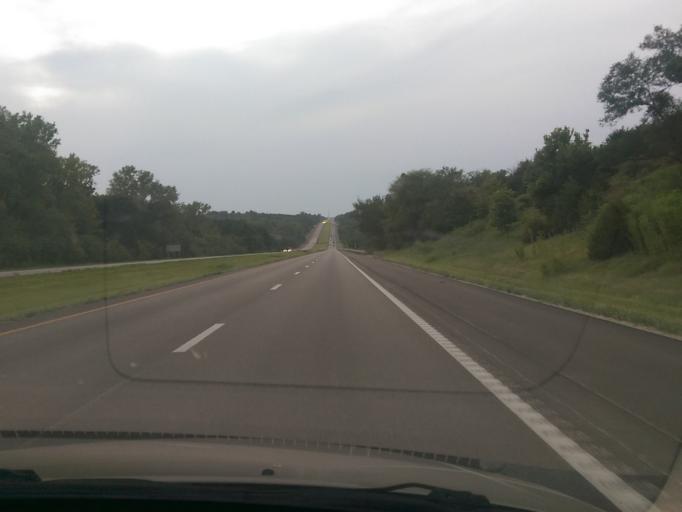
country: US
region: Missouri
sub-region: Andrew County
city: Savannah
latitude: 39.8994
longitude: -94.8774
